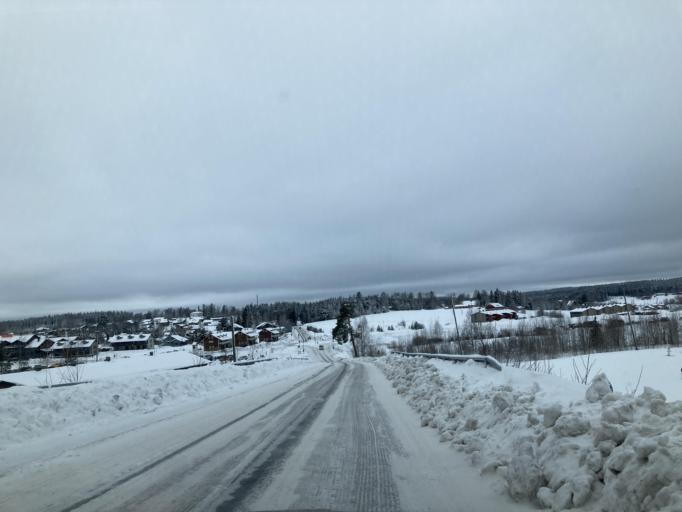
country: FI
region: Central Finland
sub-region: Jaemsae
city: Jaemsae
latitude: 61.8805
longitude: 25.3053
